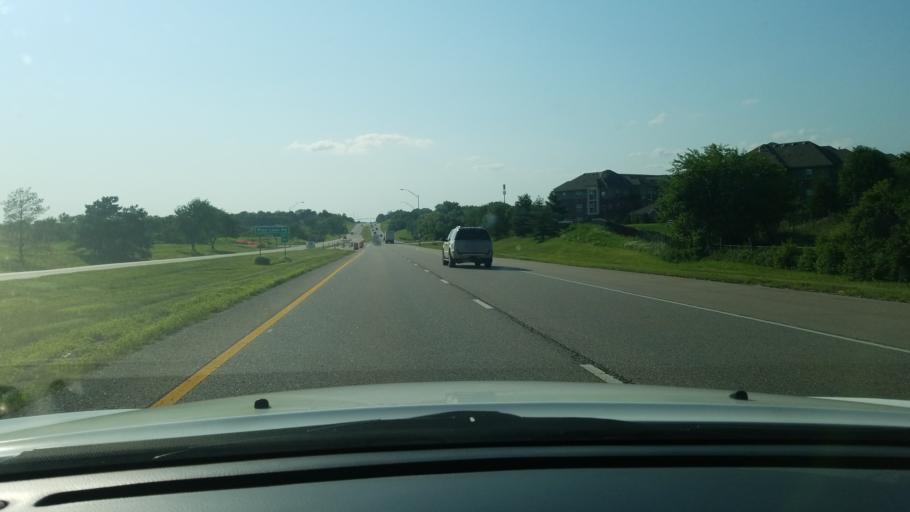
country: US
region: Nebraska
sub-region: Lancaster County
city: Lincoln
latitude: 40.7409
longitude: -96.6155
